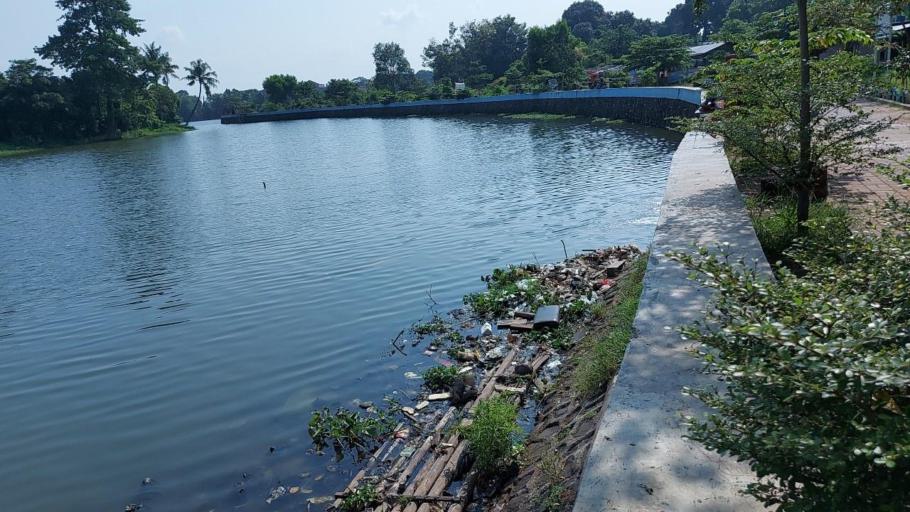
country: ID
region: West Java
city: Cibinong
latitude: -6.4721
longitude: 106.8565
